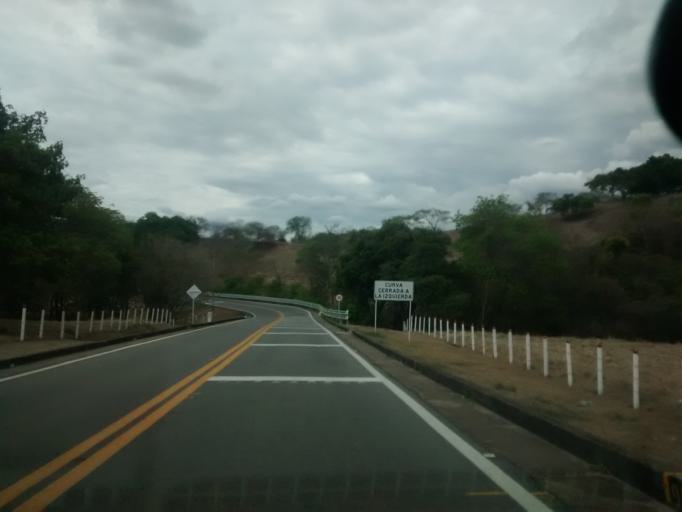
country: CO
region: Cundinamarca
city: Agua de Dios
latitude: 4.4104
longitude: -74.7093
